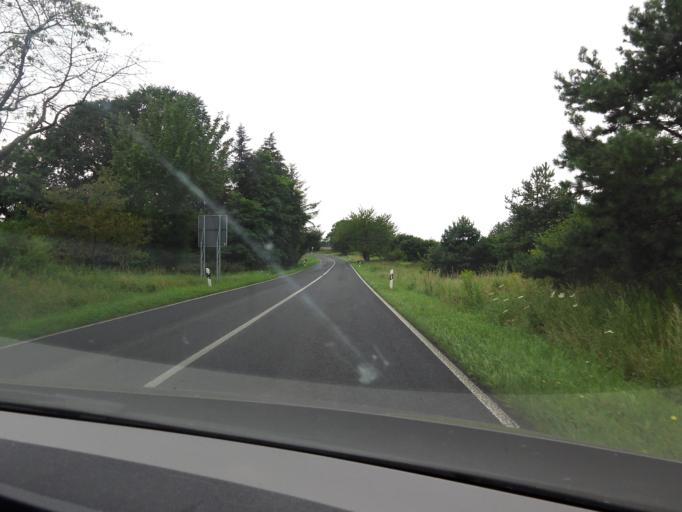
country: DE
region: Brandenburg
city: Lychen
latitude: 53.2099
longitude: 13.2727
